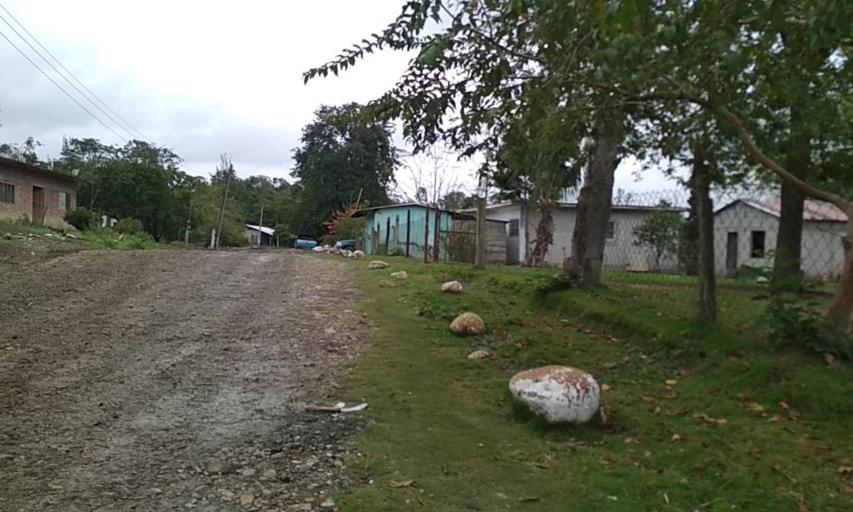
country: MX
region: Puebla
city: Espinal
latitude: 20.3205
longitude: -97.4178
